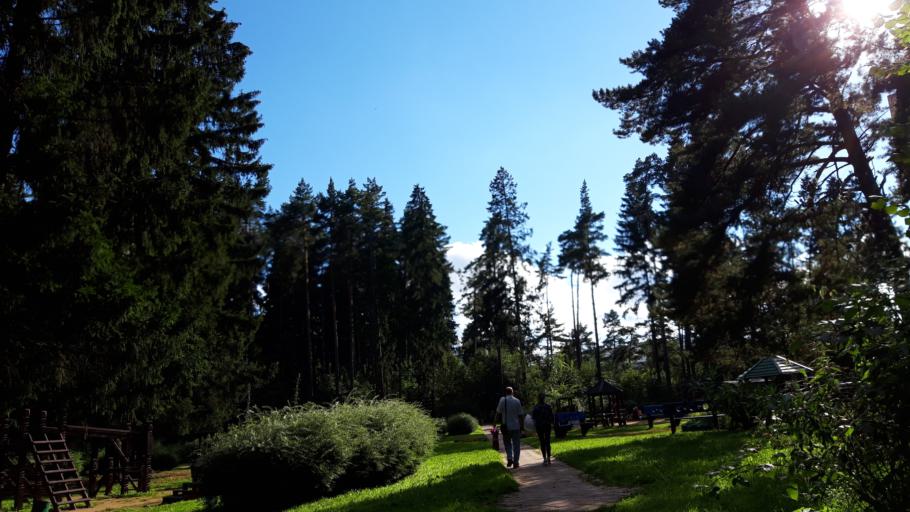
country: RU
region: Moscow
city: Zelenograd
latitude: 55.9864
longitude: 37.1945
